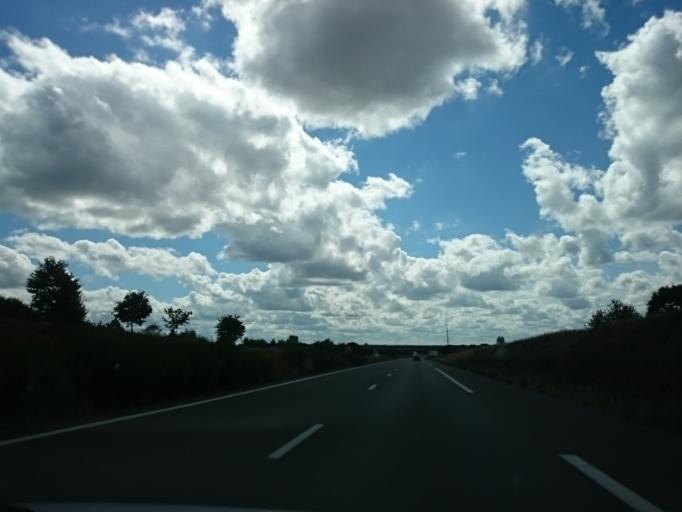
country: FR
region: Pays de la Loire
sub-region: Departement de Maine-et-Loire
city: Saint-Leger-des-Bois
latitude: 47.4599
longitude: -0.6989
